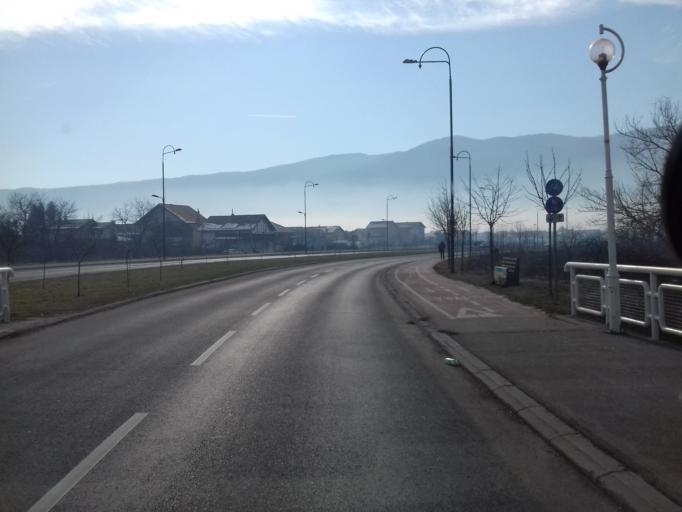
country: BA
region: Federation of Bosnia and Herzegovina
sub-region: Kanton Sarajevo
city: Sarajevo
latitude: 43.8228
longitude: 18.3194
